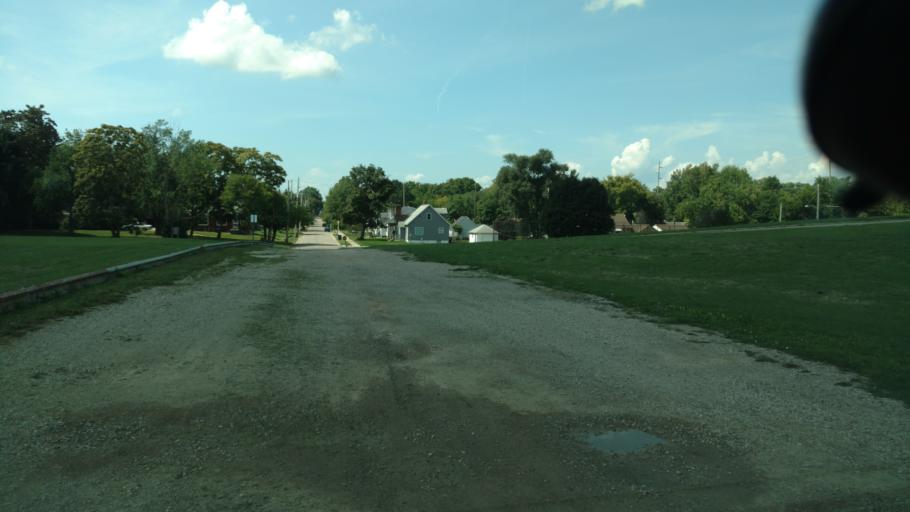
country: US
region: Michigan
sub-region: Ingham County
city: Lansing
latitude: 42.7567
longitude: -84.5468
